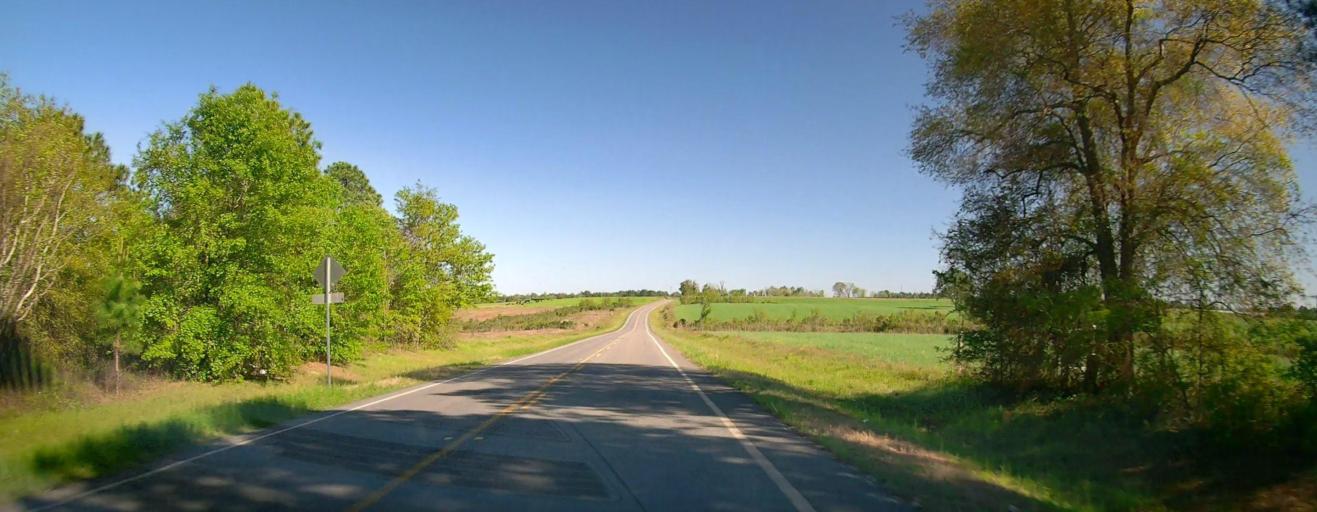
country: US
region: Georgia
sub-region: Wilcox County
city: Rochelle
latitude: 31.9880
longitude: -83.4642
